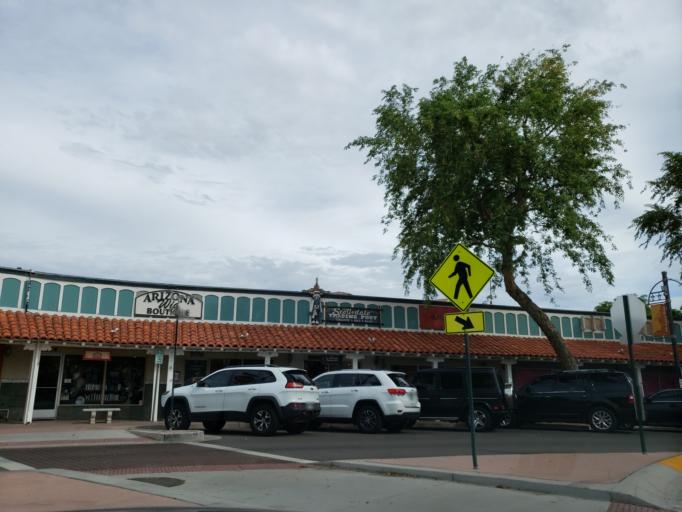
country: US
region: Arizona
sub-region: Maricopa County
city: Scottsdale
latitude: 33.4981
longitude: -111.9289
